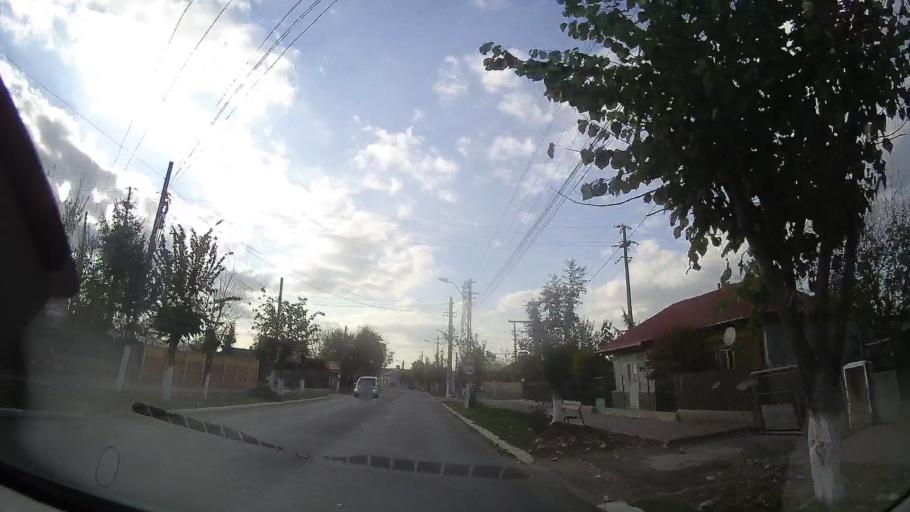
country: RO
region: Constanta
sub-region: Comuna Negru Voda
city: Negru Voda
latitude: 43.8194
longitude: 28.2218
